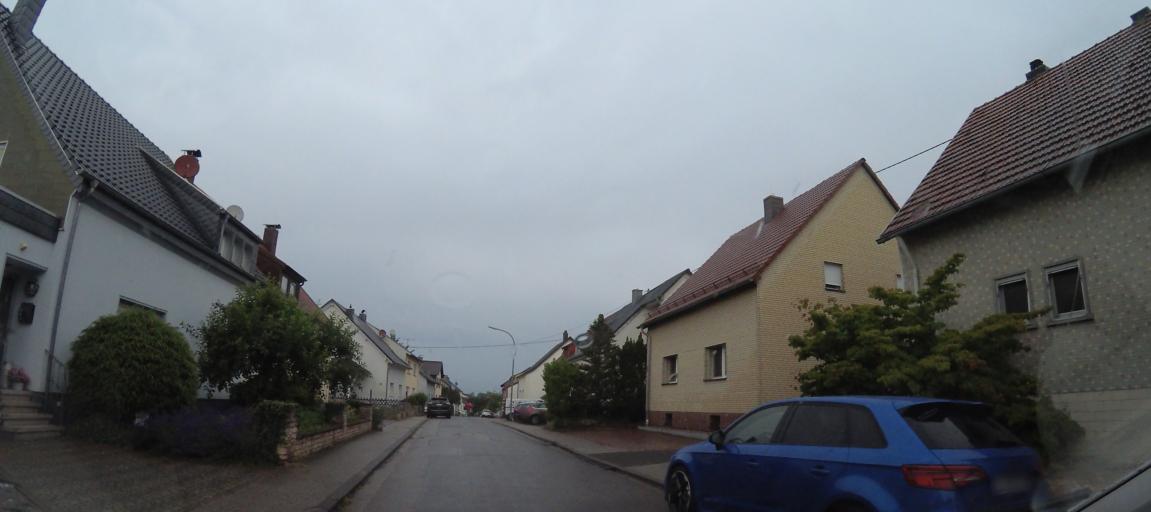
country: DE
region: Saarland
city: Wallerfangen
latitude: 49.3227
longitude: 6.7161
